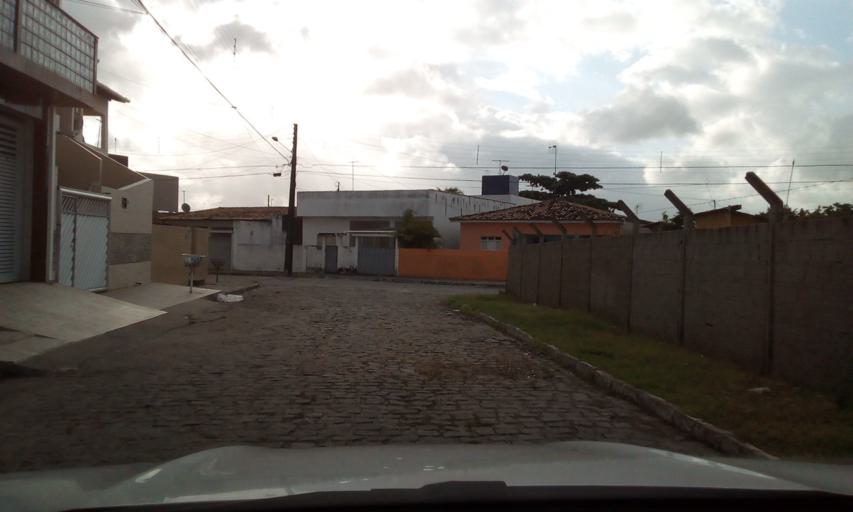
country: BR
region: Paraiba
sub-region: Joao Pessoa
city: Joao Pessoa
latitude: -7.1812
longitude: -34.8450
